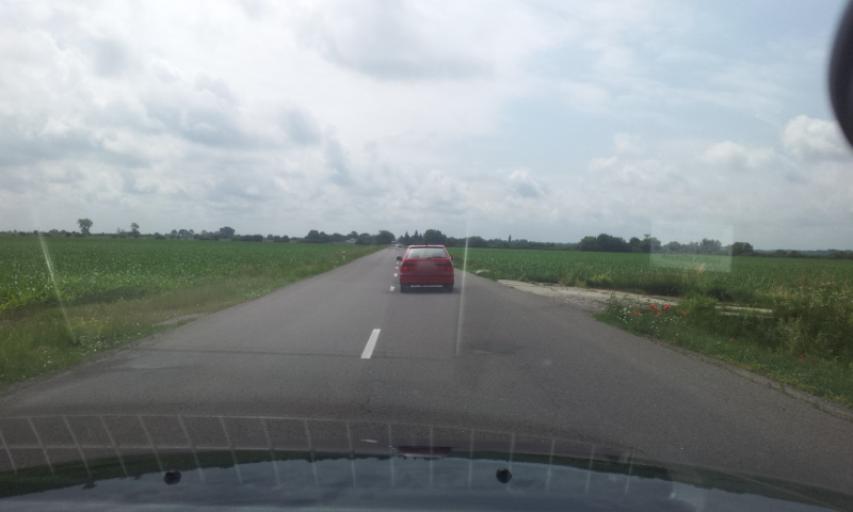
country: SK
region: Kosicky
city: Michalovce
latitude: 48.7071
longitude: 21.9652
